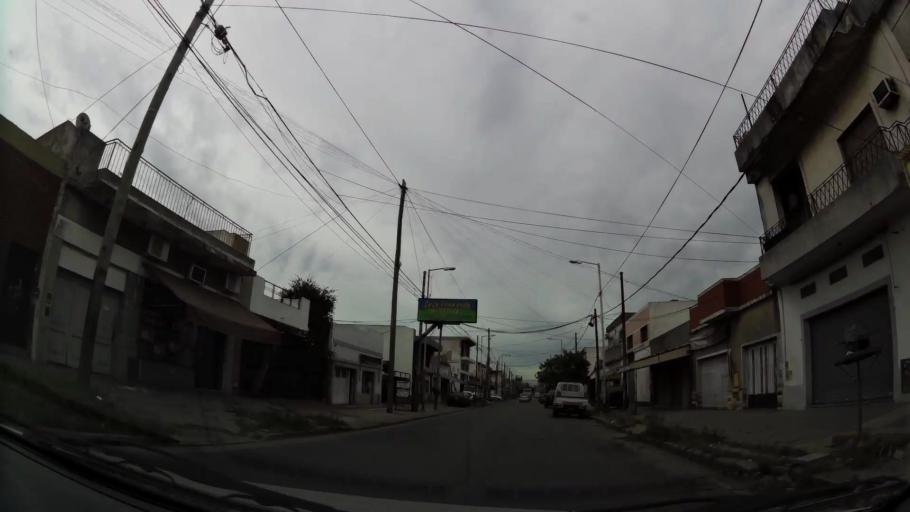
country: AR
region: Buenos Aires
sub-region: Partido de Lanus
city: Lanus
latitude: -34.6903
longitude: -58.3688
